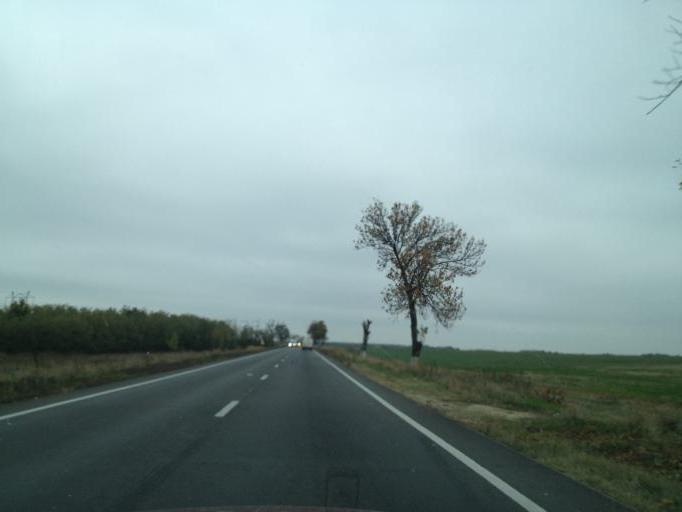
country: RO
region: Arges
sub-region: Comuna Sapata
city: Martesti
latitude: 44.7110
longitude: 24.7900
